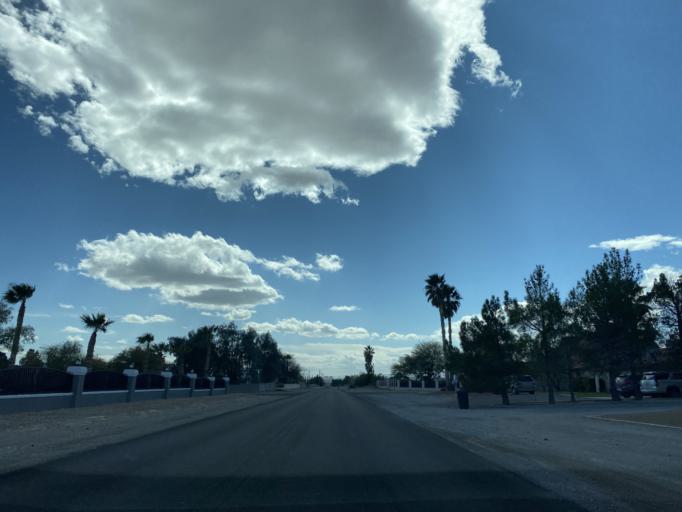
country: US
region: Nevada
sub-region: Clark County
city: Summerlin South
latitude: 36.2691
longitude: -115.2882
